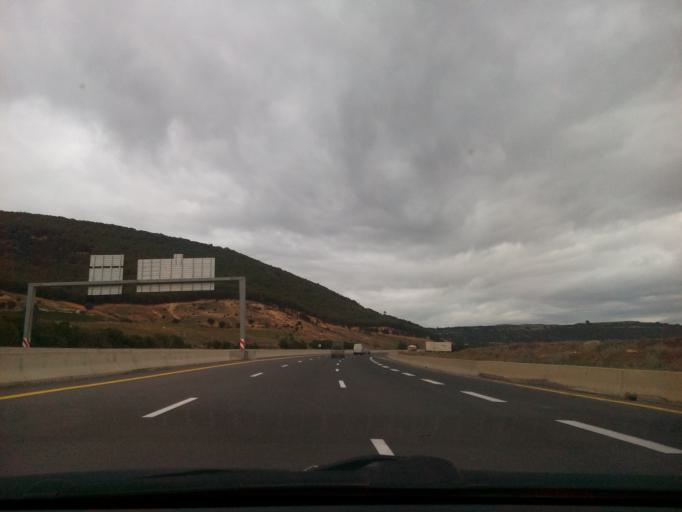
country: DZ
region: Sidi Bel Abbes
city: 'Ain el Berd
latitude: 35.3839
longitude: -0.4988
